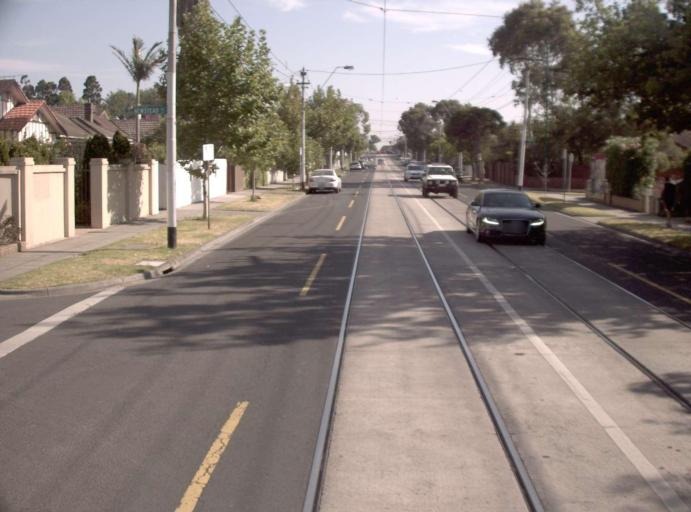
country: AU
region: Victoria
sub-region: Glen Eira
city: Caulfield
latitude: -37.8836
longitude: 145.0226
